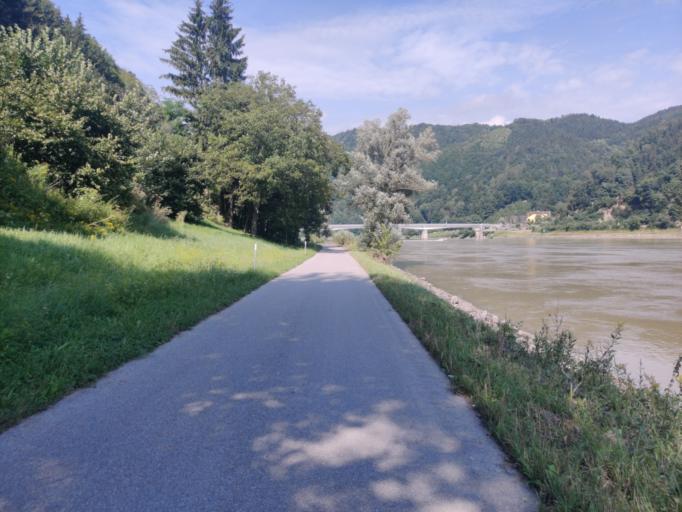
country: AT
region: Upper Austria
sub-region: Politischer Bezirk Perg
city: Bad Kreuzen
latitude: 48.2077
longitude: 14.8520
